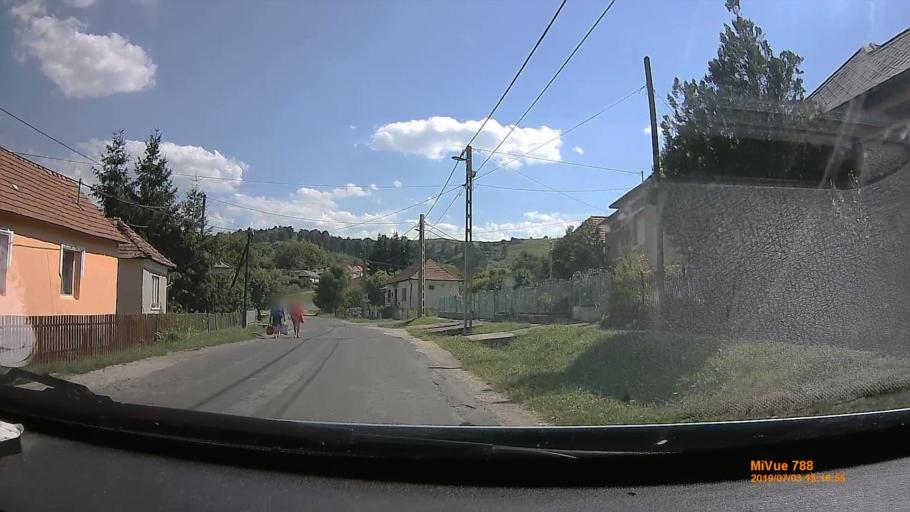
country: HU
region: Borsod-Abauj-Zemplen
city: Farkaslyuk
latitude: 48.2086
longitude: 20.3984
